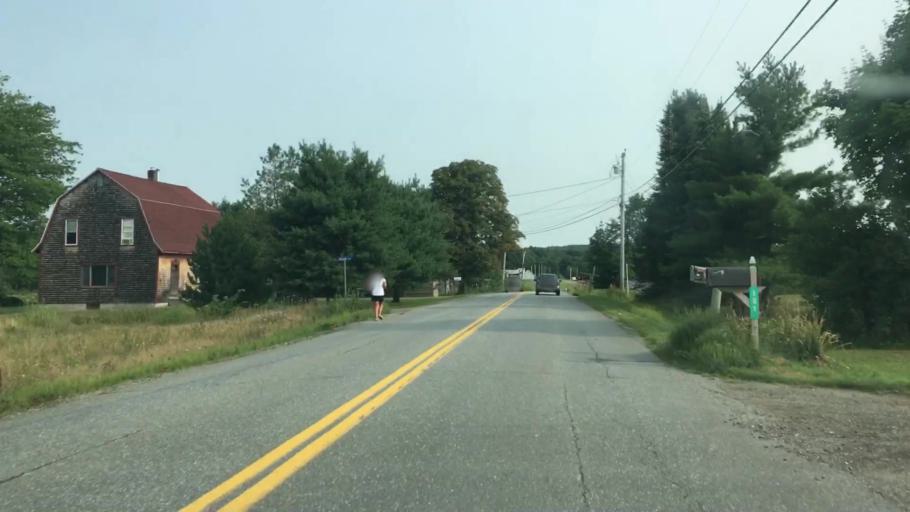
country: US
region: Maine
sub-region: Kennebec County
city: Chelsea
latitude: 44.3025
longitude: -69.6968
